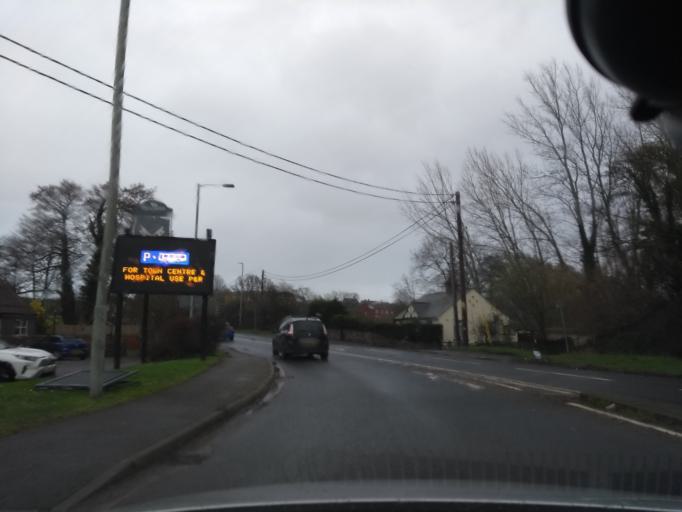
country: GB
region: England
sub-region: Somerset
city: Taunton
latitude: 51.0310
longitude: -3.1359
